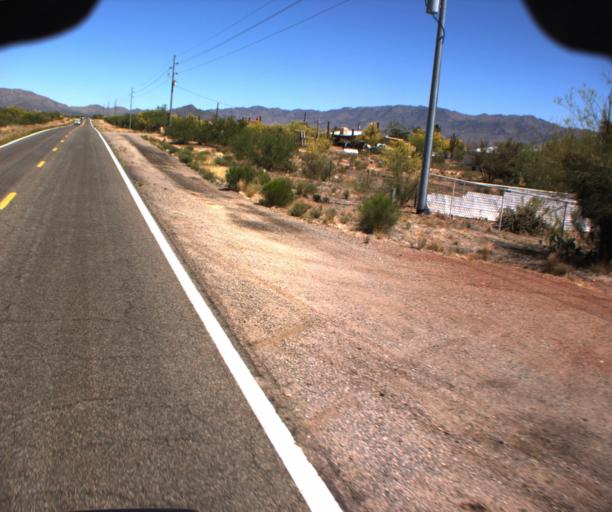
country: US
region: Arizona
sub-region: Yavapai County
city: Congress
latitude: 34.1177
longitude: -112.8352
